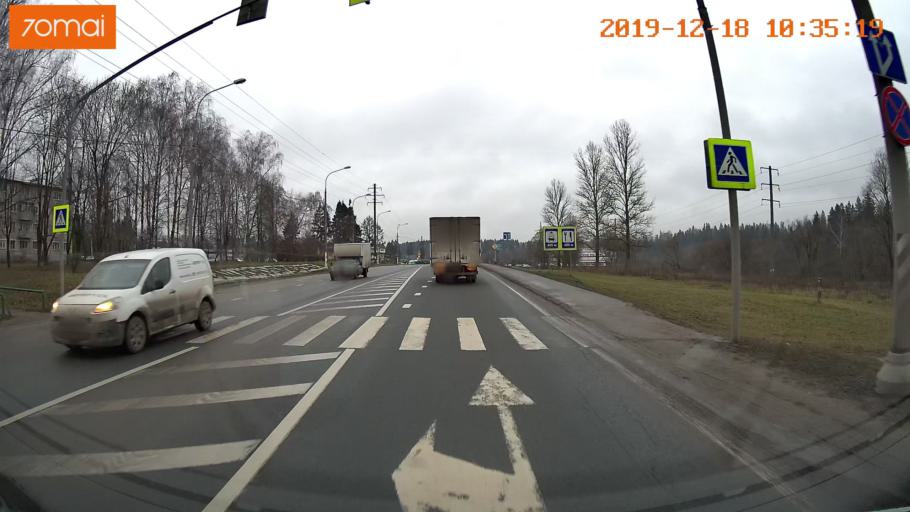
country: RU
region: Moskovskaya
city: Troitsk
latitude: 55.4137
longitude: 37.1950
